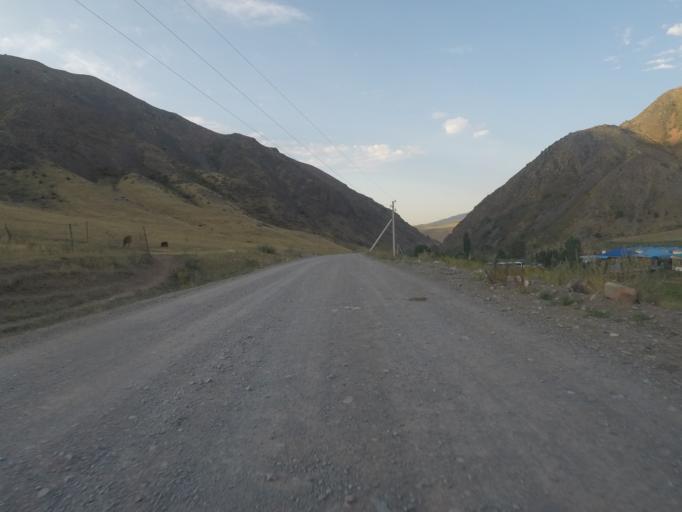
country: KG
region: Chuy
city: Bishkek
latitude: 42.6772
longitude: 74.6540
